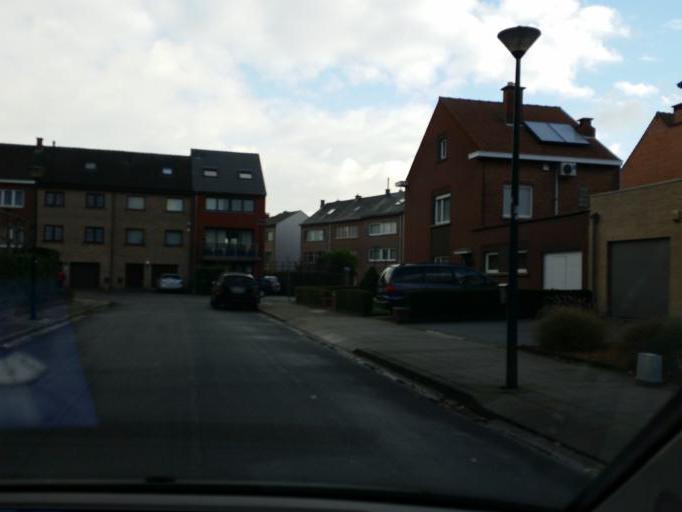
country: BE
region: Flanders
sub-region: Provincie Vlaams-Brabant
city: Vilvoorde
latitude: 50.9288
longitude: 4.4442
